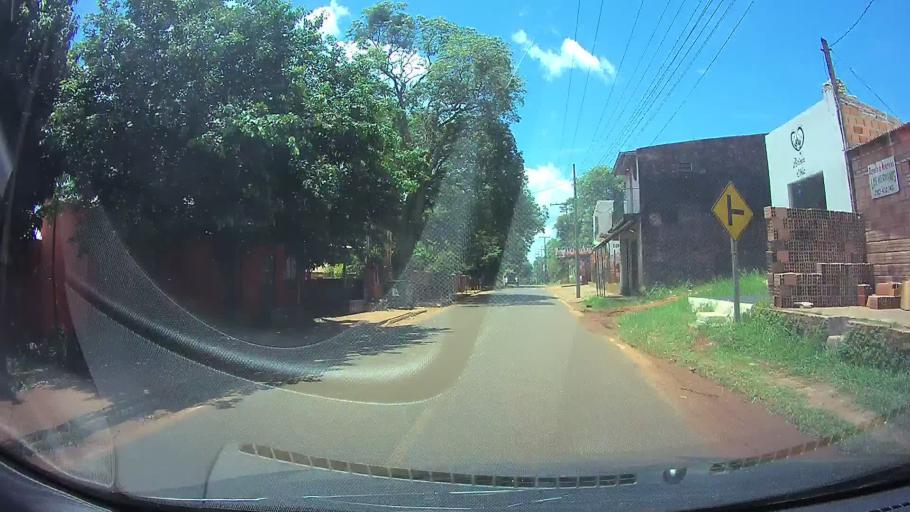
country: PY
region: Central
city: Itaugua
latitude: -25.3779
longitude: -57.3662
